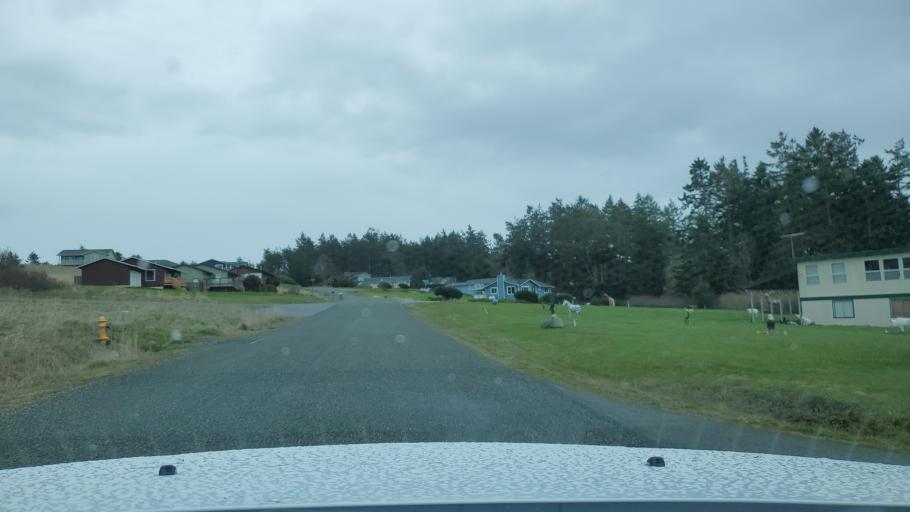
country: US
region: Washington
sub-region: Island County
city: Coupeville
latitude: 48.2333
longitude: -122.7613
